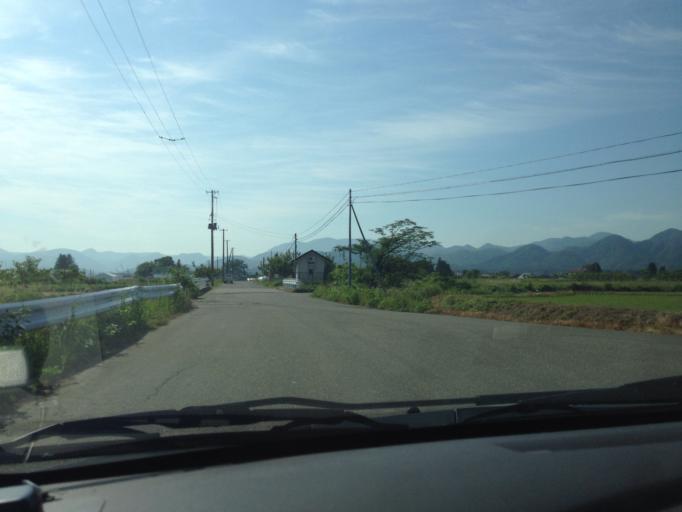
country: JP
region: Fukushima
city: Kitakata
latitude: 37.4509
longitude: 139.8245
